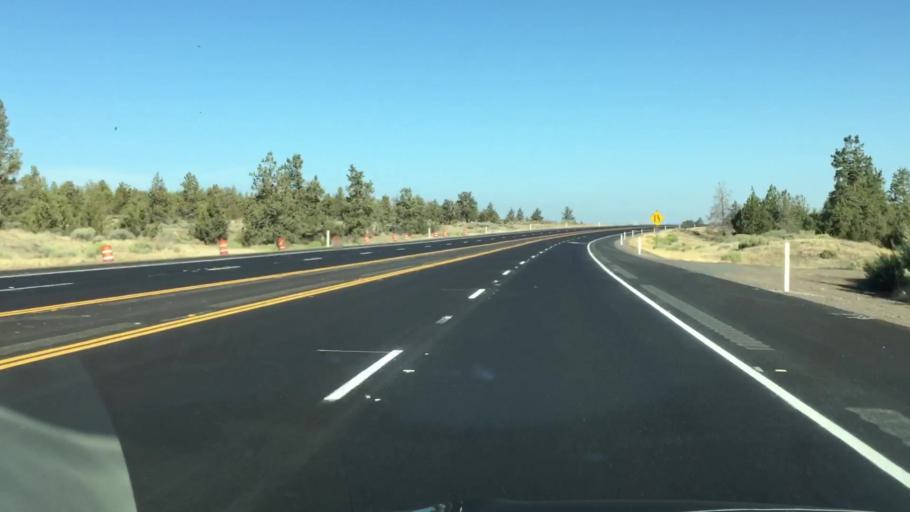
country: US
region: Oregon
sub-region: Deschutes County
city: Terrebonne
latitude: 44.3952
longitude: -121.1956
